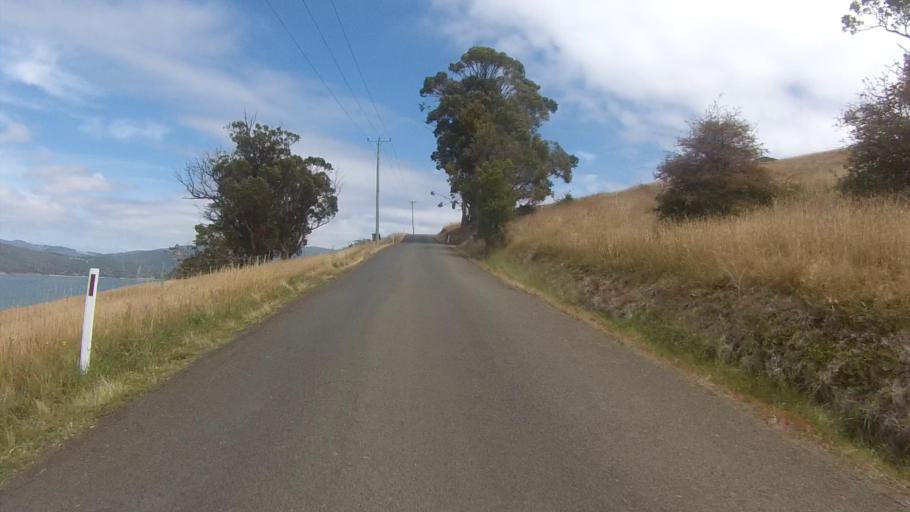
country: AU
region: Tasmania
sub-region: Kingborough
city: Blackmans Bay
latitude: -43.0570
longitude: 147.3235
